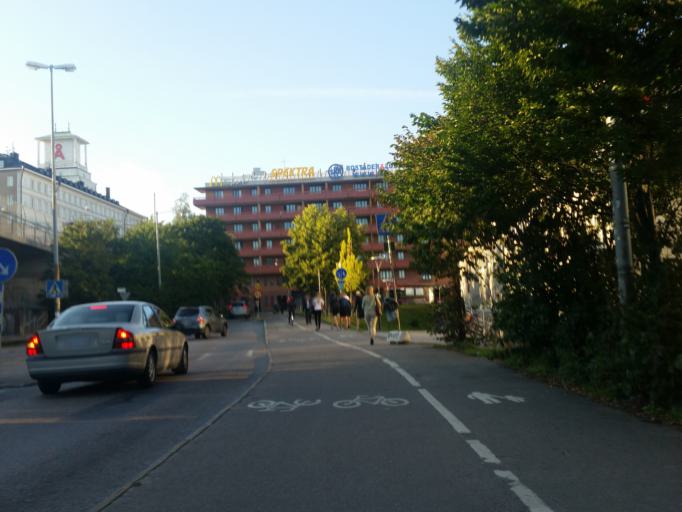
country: SE
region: Stockholm
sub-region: Stockholms Kommun
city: Arsta
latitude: 59.3056
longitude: 18.0785
